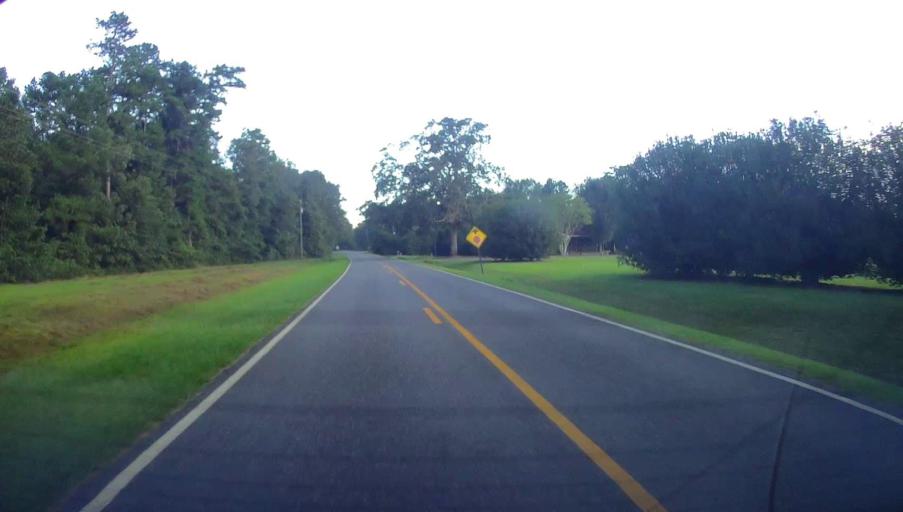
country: US
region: Georgia
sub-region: Pulaski County
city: Hawkinsville
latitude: 32.2977
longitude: -83.5528
